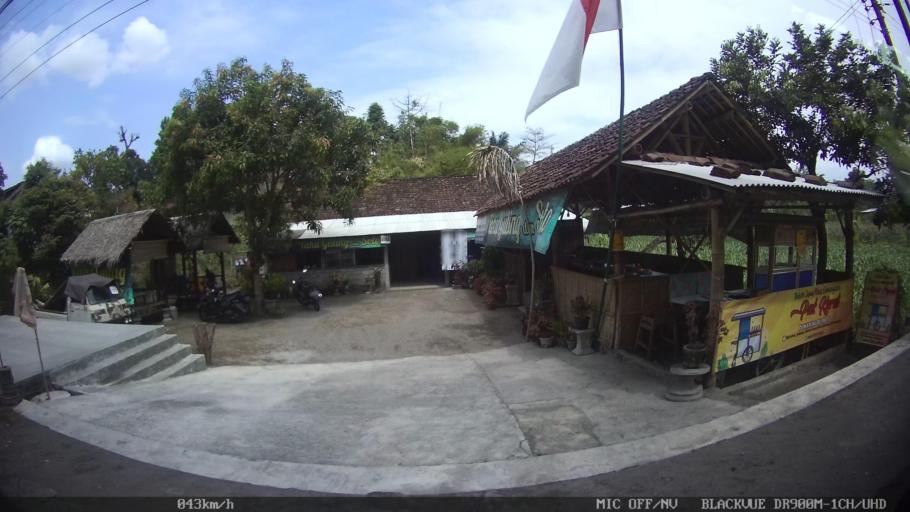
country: ID
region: Central Java
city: Candi Prambanan
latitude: -7.7310
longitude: 110.4623
